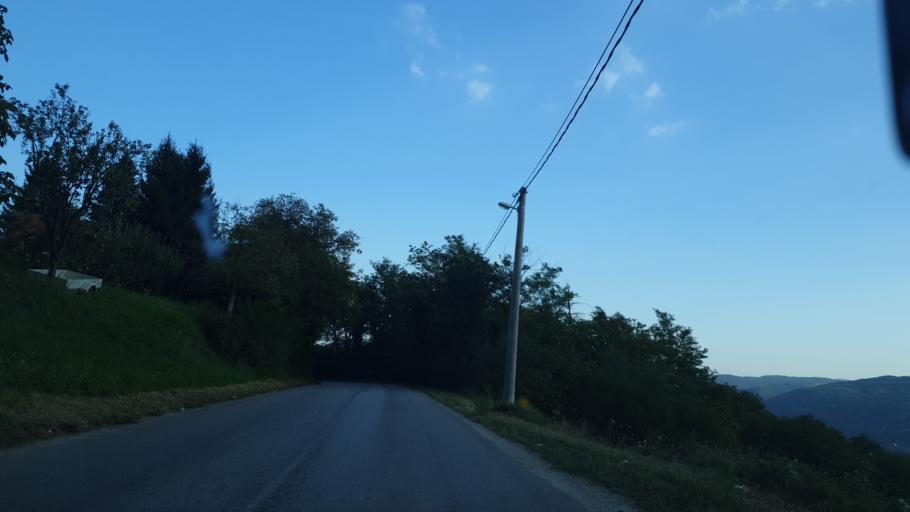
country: RS
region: Central Serbia
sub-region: Zlatiborski Okrug
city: Uzice
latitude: 43.8628
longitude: 19.8949
